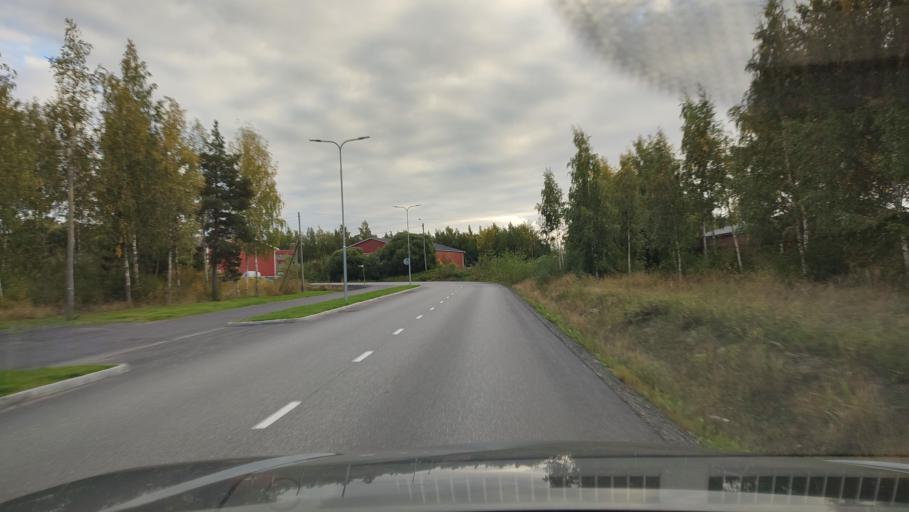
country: FI
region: Ostrobothnia
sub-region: Sydosterbotten
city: Kristinestad
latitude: 62.2635
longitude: 21.3834
